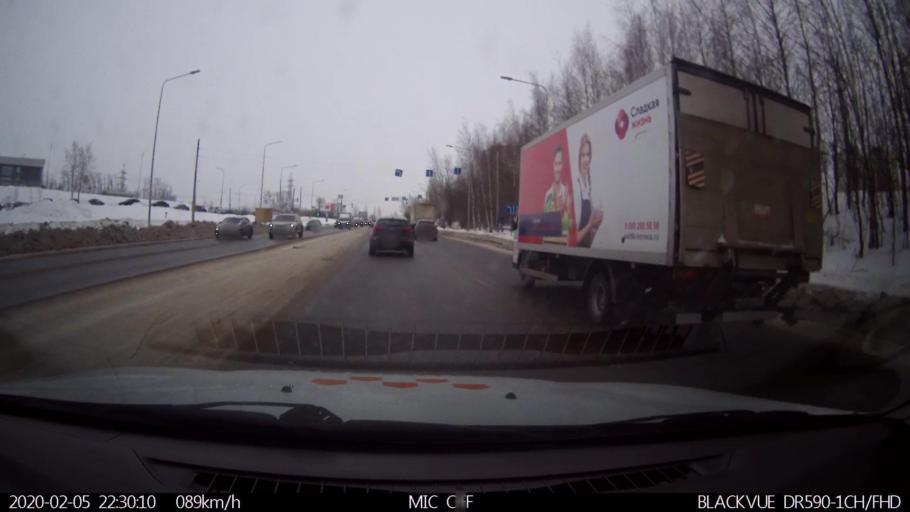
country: RU
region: Nizjnij Novgorod
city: Imeni Stepana Razina
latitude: 54.7444
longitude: 44.1559
